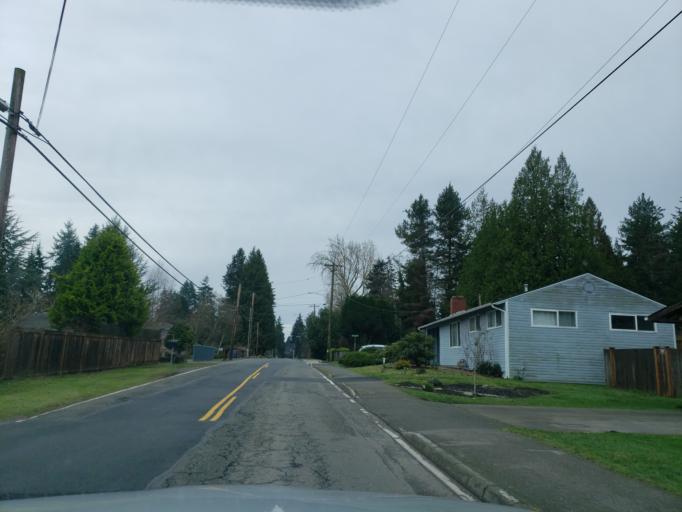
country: US
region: Washington
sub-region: Snohomish County
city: Meadowdale
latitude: 47.8274
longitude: -122.3413
